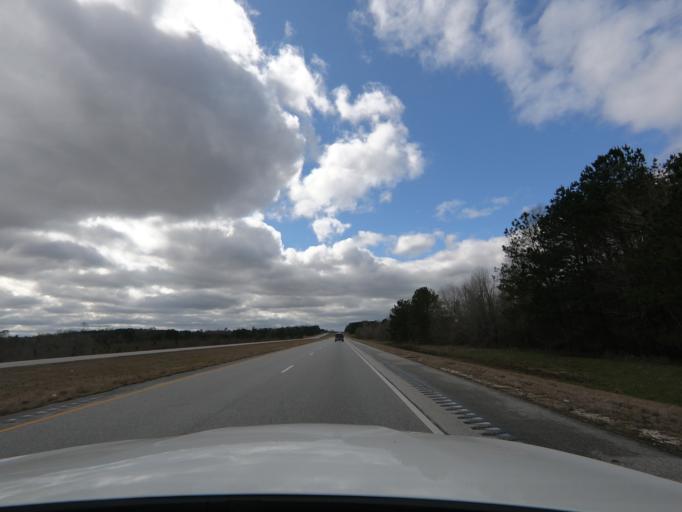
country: US
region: Alabama
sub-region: Russell County
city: Ladonia
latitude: 32.3789
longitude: -85.0859
